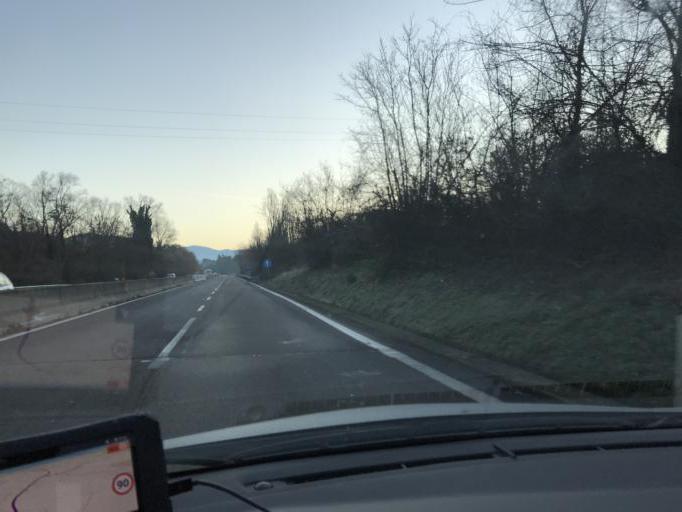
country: IT
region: Umbria
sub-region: Provincia di Terni
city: Terni
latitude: 42.5846
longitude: 12.6521
